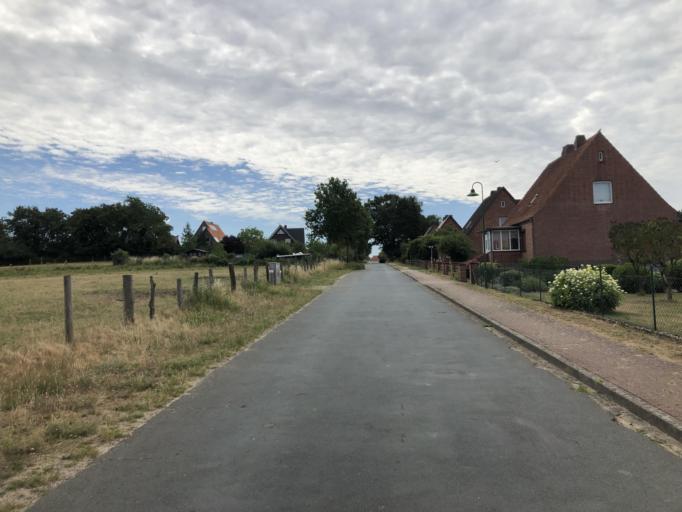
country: DE
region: Lower Saxony
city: Bleckede
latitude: 53.2602
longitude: 10.7567
